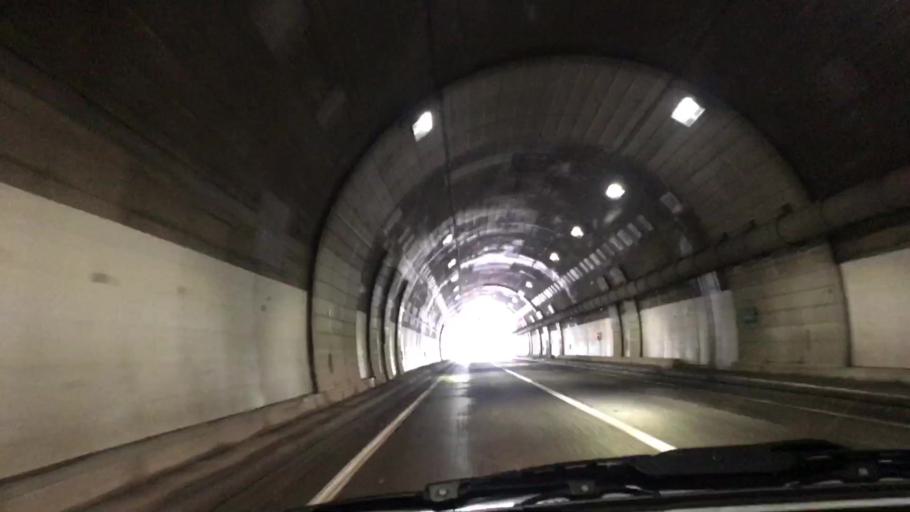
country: JP
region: Hokkaido
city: Otofuke
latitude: 43.3689
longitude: 143.2088
